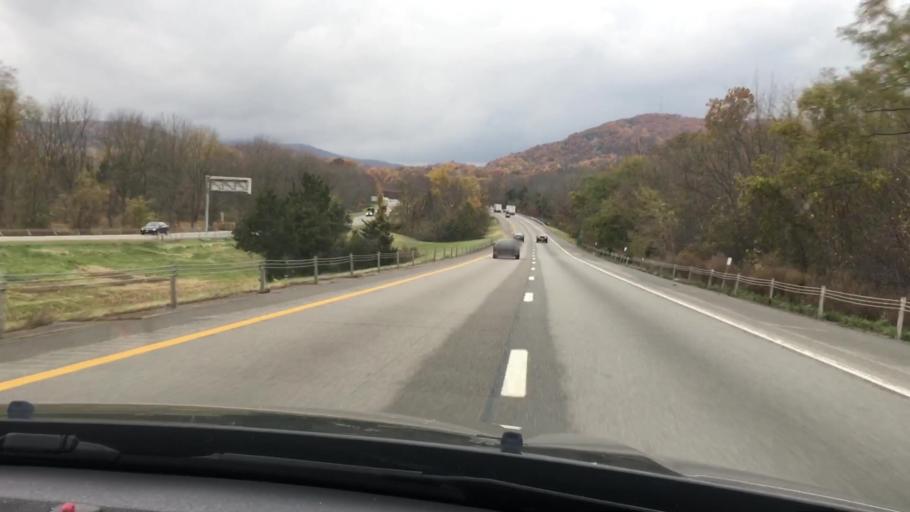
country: US
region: New York
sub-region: Dutchess County
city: Brinckerhoff
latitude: 41.5323
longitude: -73.8381
